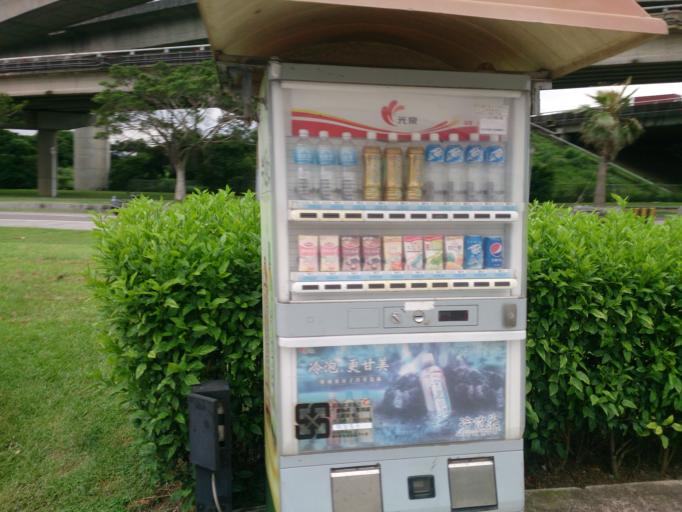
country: TW
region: Taipei
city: Taipei
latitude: 25.0742
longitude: 121.5302
